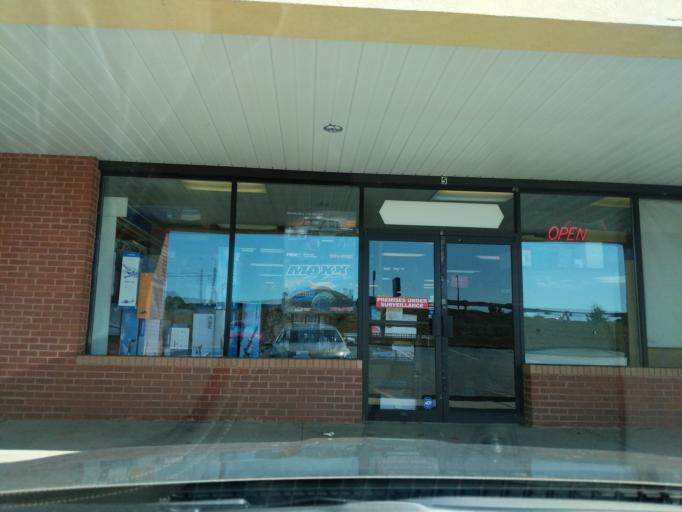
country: US
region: Georgia
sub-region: Columbia County
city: Martinez
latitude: 33.5029
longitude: -82.0878
